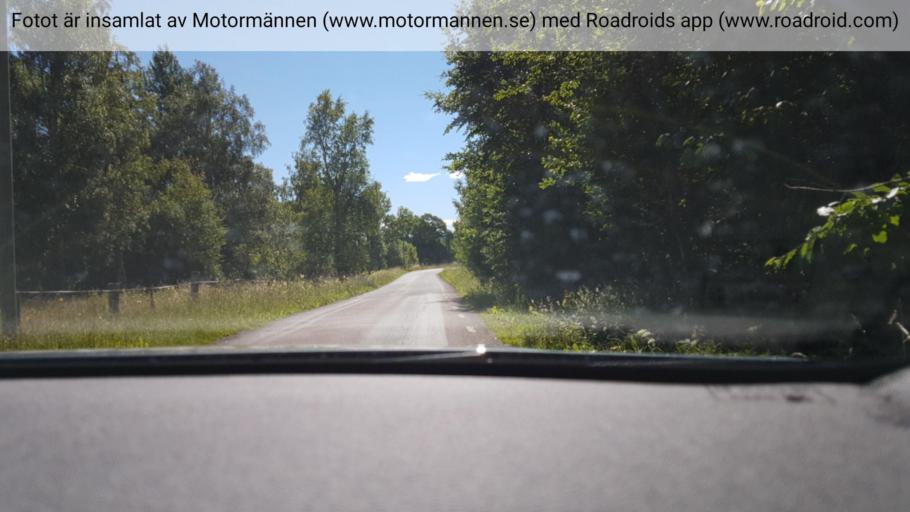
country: SE
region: Vaestra Goetaland
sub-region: Falkopings Kommun
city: Akarp
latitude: 58.2632
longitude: 13.6498
